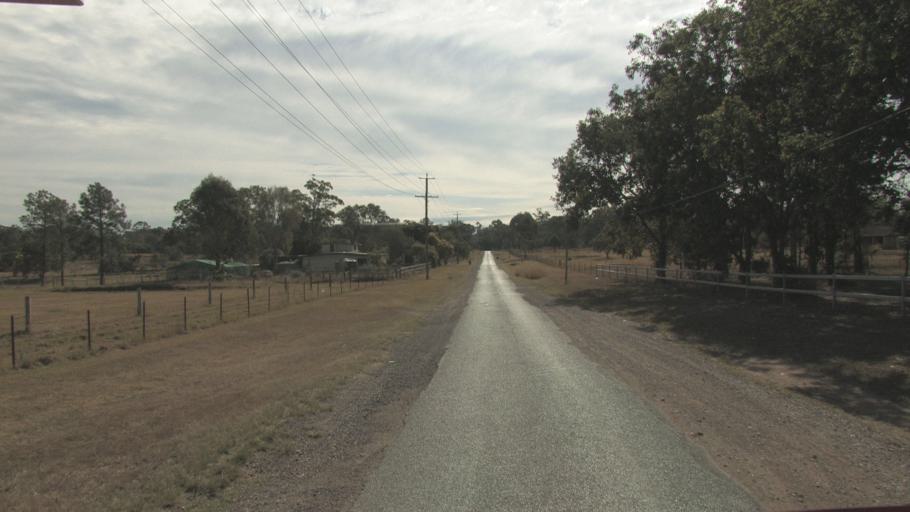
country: AU
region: Queensland
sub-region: Logan
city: North Maclean
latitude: -27.7793
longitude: 153.0078
